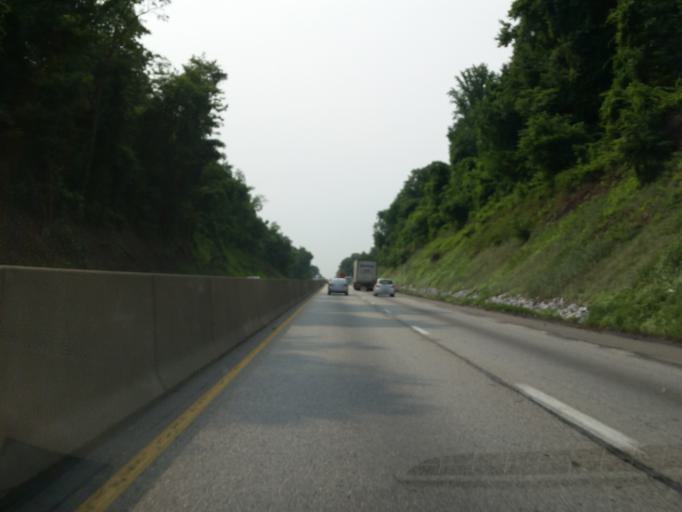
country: US
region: Pennsylvania
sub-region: York County
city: Valley Green
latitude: 40.1011
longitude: -76.7776
